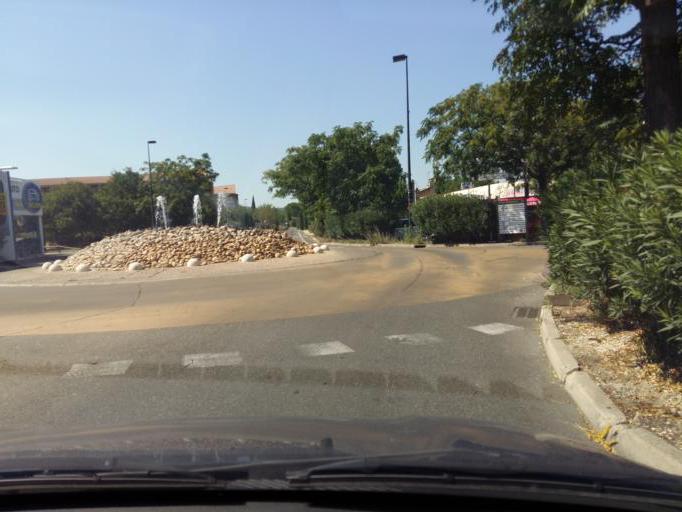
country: FR
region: Languedoc-Roussillon
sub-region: Departement du Gard
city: Les Angles
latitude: 43.9586
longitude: 4.7684
